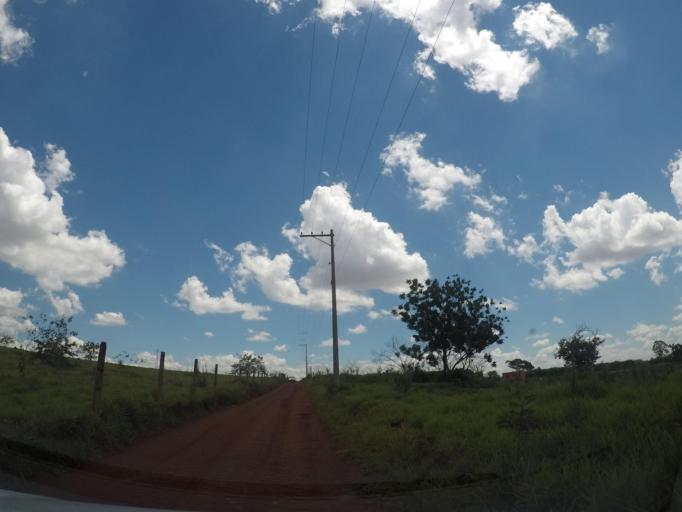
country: BR
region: Sao Paulo
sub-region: Hortolandia
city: Hortolandia
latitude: -22.8415
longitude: -47.2414
